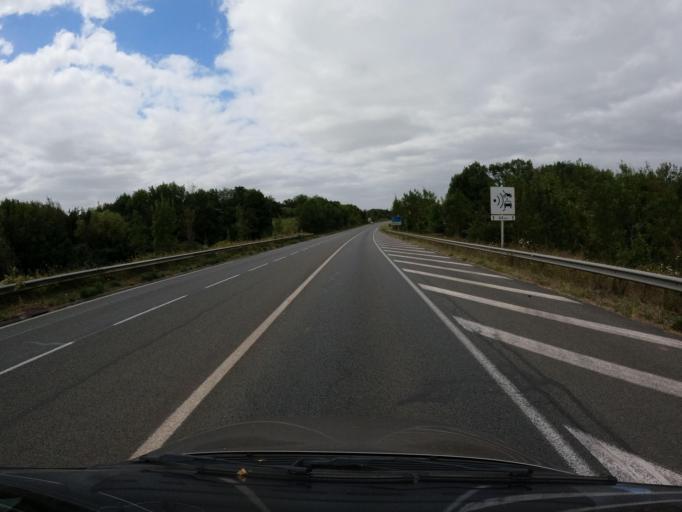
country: FR
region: Poitou-Charentes
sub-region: Departement des Deux-Sevres
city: Melle
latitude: 46.2101
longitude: -0.1516
